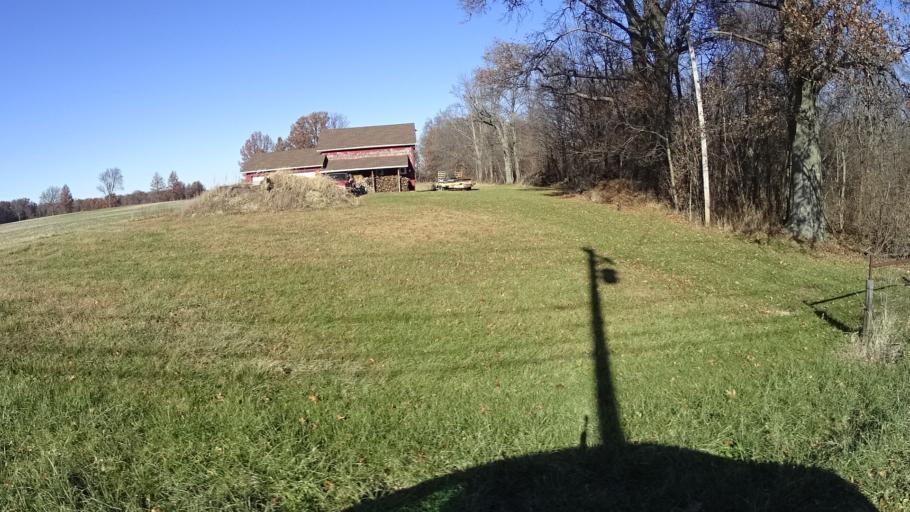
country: US
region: Ohio
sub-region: Lorain County
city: Grafton
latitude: 41.3003
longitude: -82.0958
